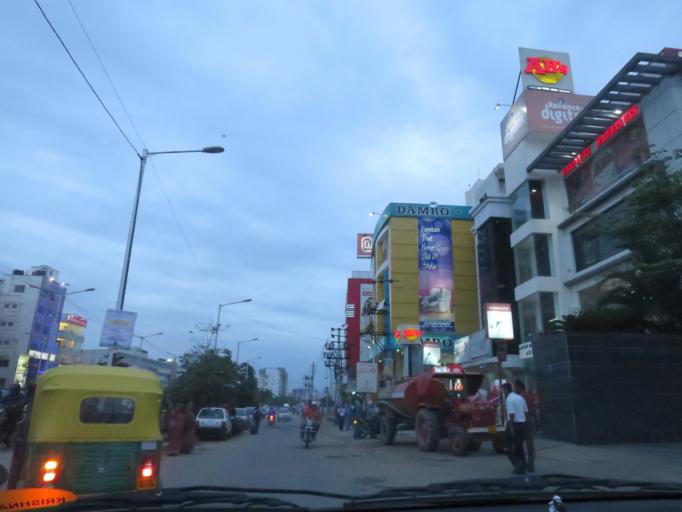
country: IN
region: Karnataka
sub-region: Bangalore Urban
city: Bangalore
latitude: 12.9501
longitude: 77.6993
